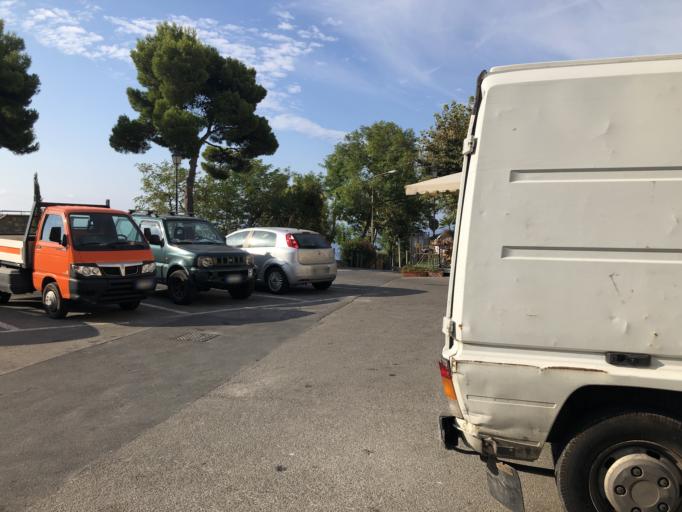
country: IT
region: Liguria
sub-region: Provincia di Imperia
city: Cipressa
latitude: 43.8515
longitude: 7.9304
